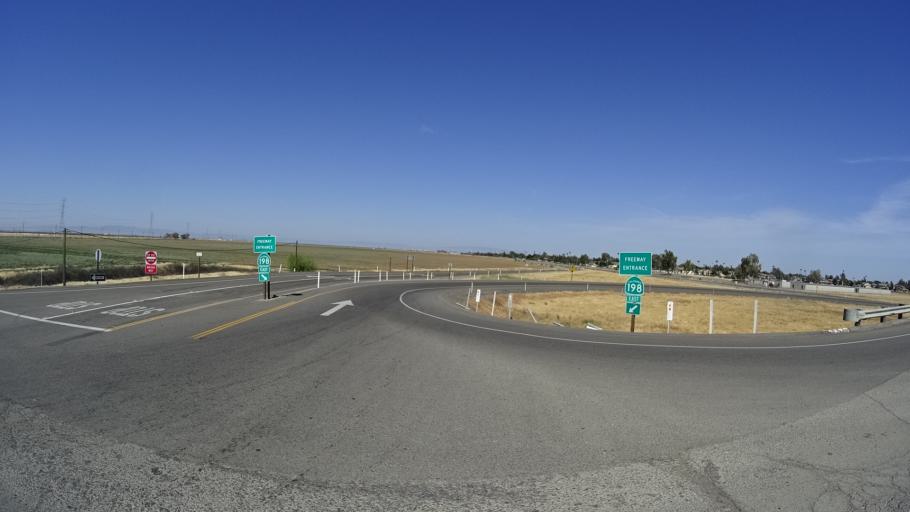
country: US
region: California
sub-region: Kings County
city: Lemoore Station
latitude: 36.2542
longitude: -119.8695
